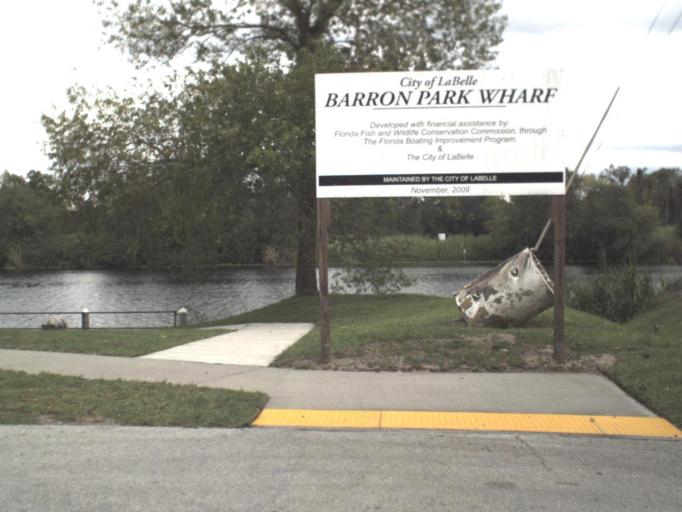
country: US
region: Florida
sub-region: Hendry County
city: LaBelle
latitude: 26.7687
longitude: -81.4361
